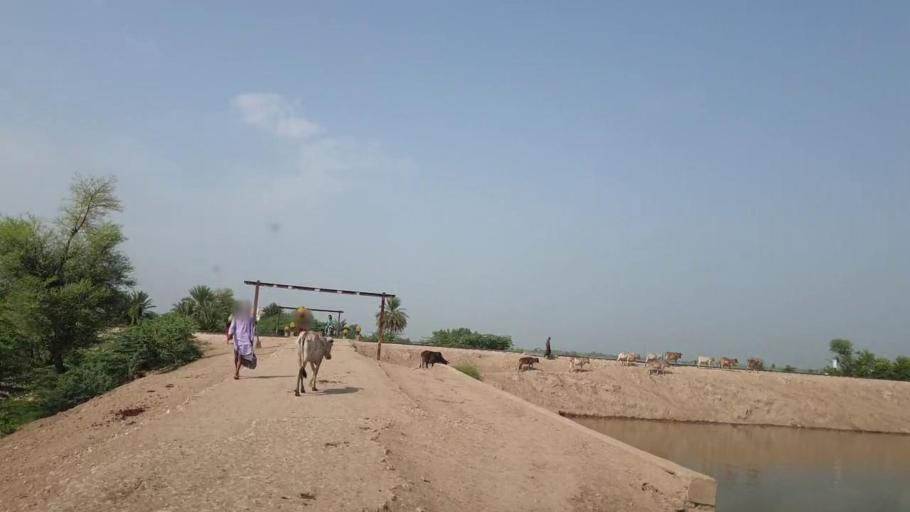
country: PK
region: Sindh
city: Lakhi
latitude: 27.8110
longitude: 68.7248
